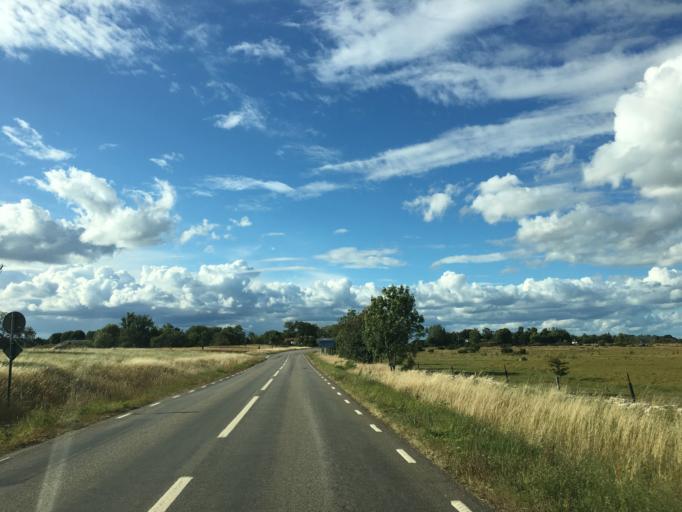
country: SE
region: Kalmar
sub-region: Morbylanga Kommun
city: Moerbylanga
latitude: 56.4411
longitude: 16.4288
